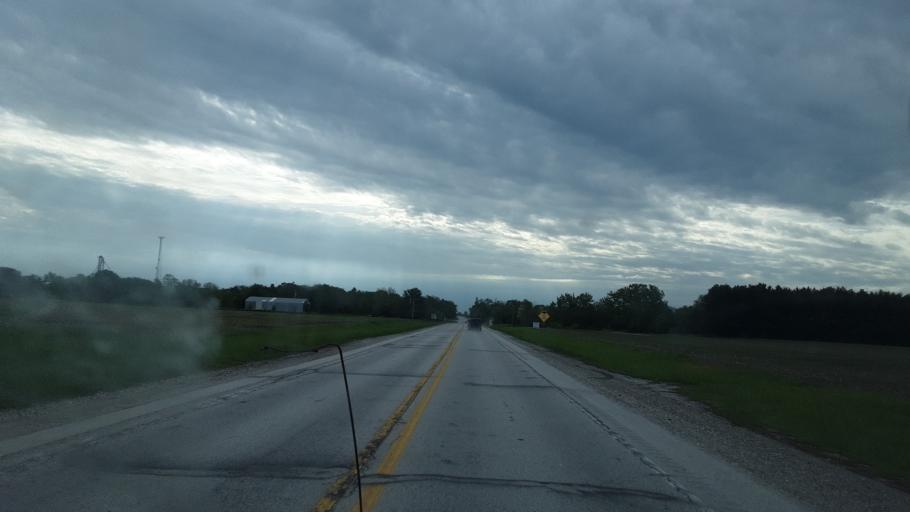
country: US
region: Illinois
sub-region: Hancock County
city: Hamilton
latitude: 40.3950
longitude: -91.2584
